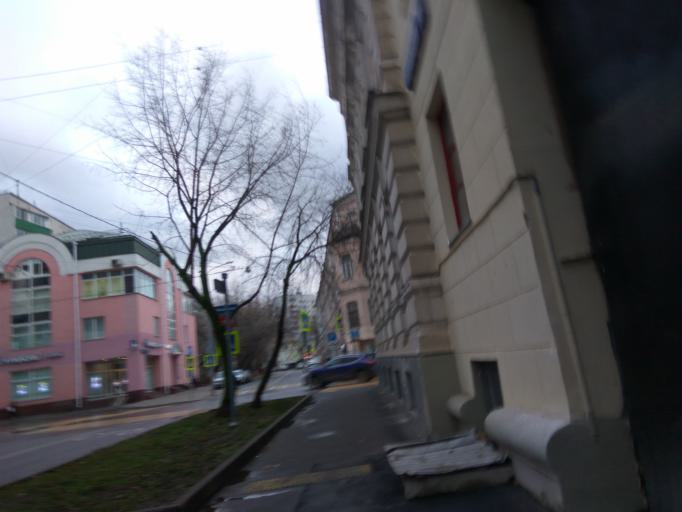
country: RU
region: Moscow
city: Taganskiy
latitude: 55.7428
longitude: 37.6627
